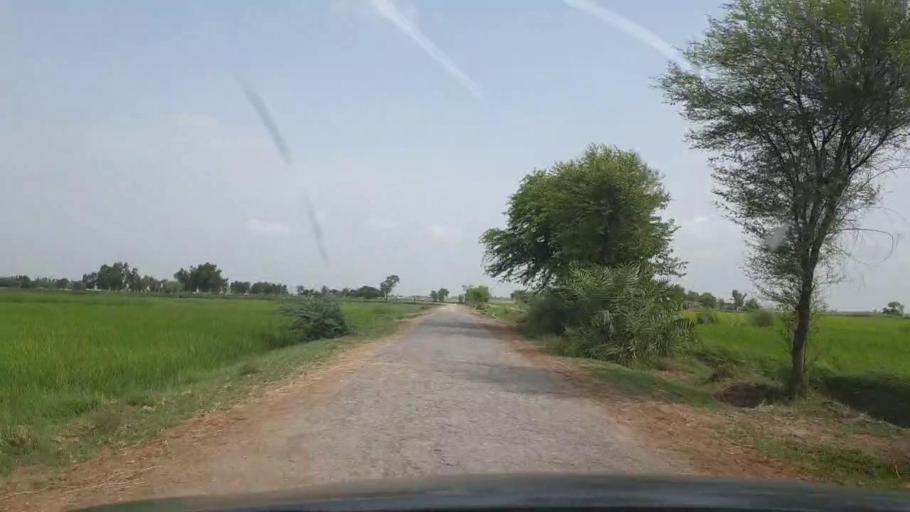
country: PK
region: Sindh
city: Ratodero
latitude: 27.8537
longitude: 68.2997
